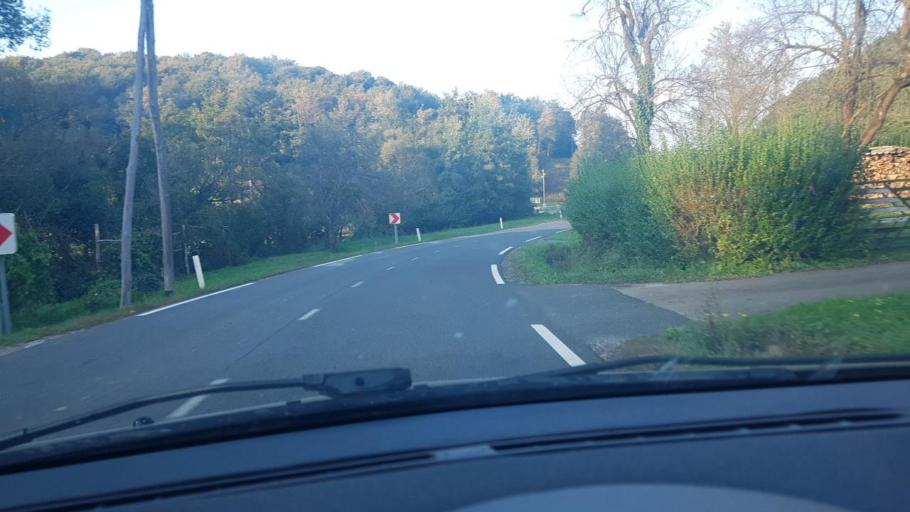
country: SI
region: Majsperk
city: Majsperk
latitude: 46.3254
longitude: 15.7203
